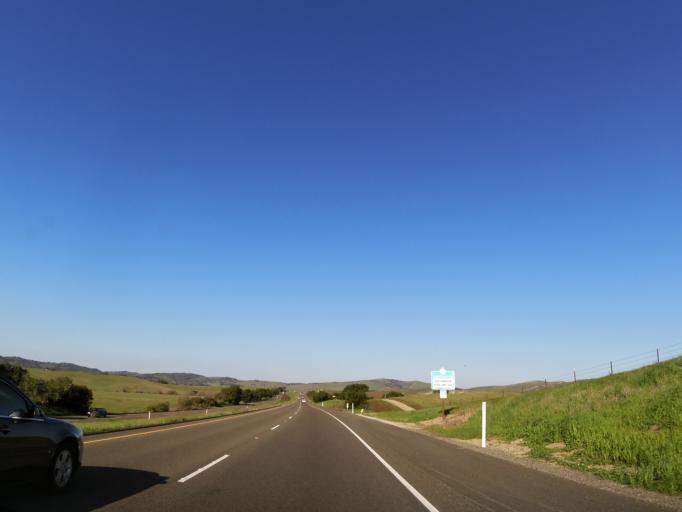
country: US
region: California
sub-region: Santa Barbara County
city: Los Alamos
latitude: 34.7850
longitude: -120.3204
